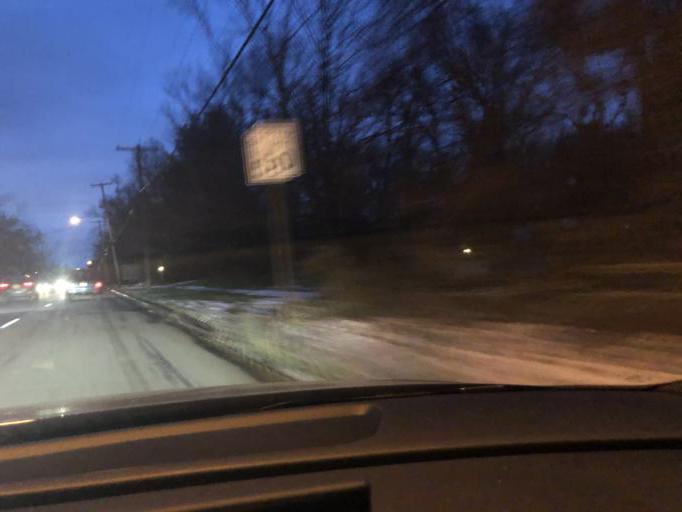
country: US
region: New Jersey
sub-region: Essex County
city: Northfield
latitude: 40.7703
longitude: -74.3504
